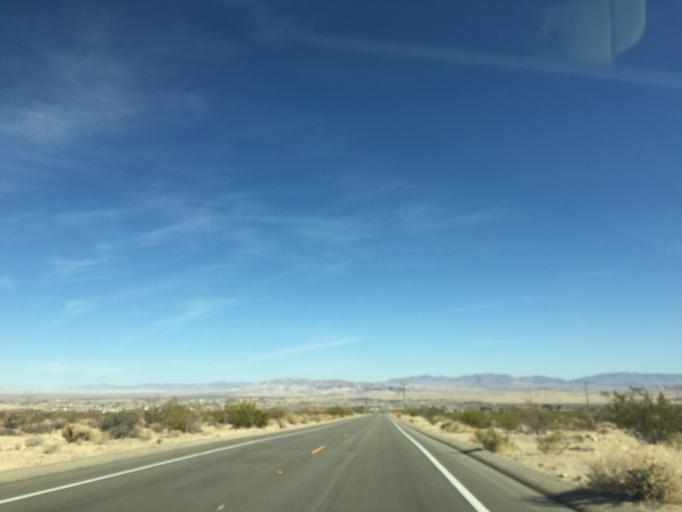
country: US
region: California
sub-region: San Bernardino County
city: Twentynine Palms
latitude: 34.1025
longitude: -116.0367
